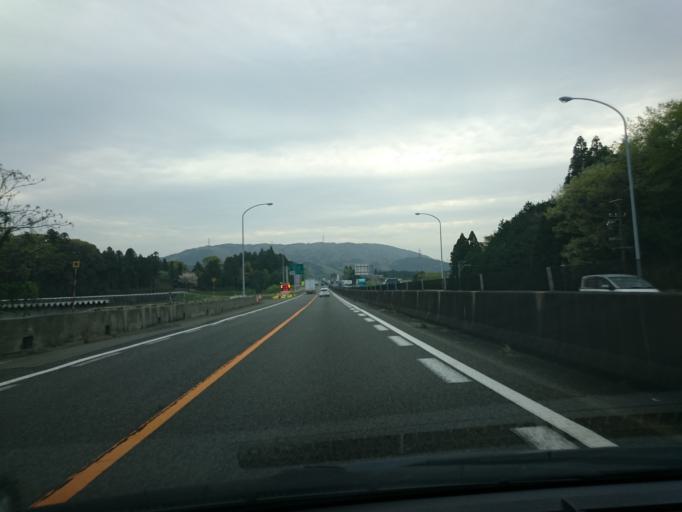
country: JP
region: Gifu
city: Tarui
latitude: 35.3549
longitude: 136.4587
